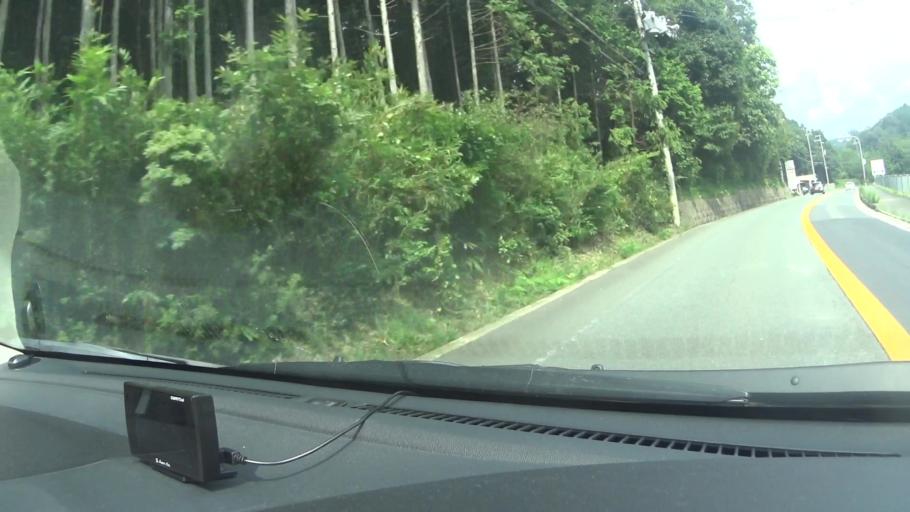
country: JP
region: Kyoto
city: Ayabe
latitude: 35.1700
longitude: 135.3599
